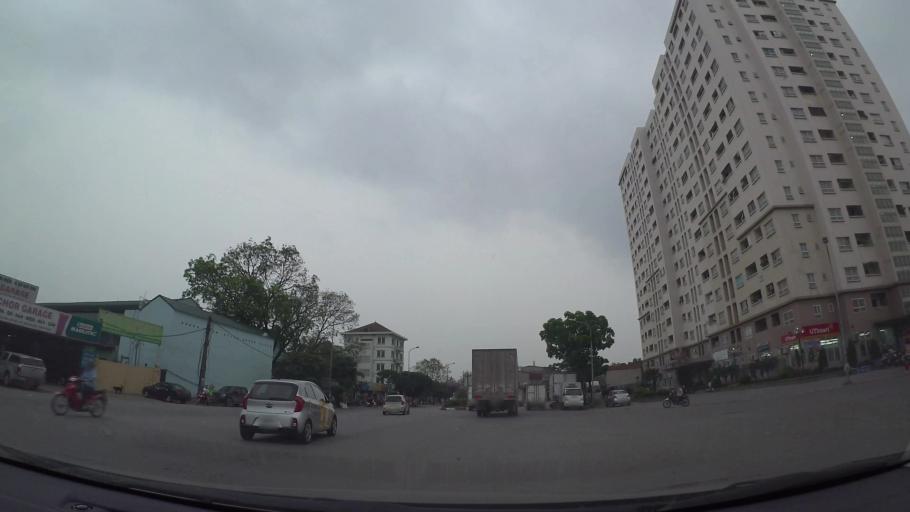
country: VN
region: Ha Noi
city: Trau Quy
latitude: 21.0393
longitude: 105.9127
